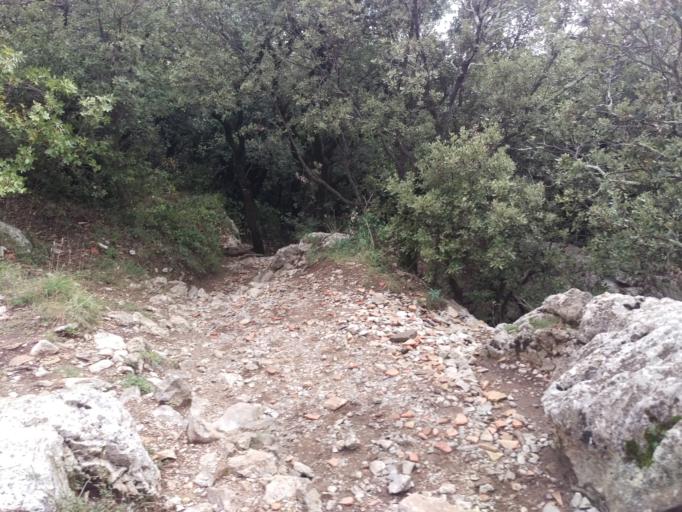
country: FR
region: Languedoc-Roussillon
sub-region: Departement de l'Herault
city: Saint-Mathieu-de-Treviers
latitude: 43.7790
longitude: 3.8115
